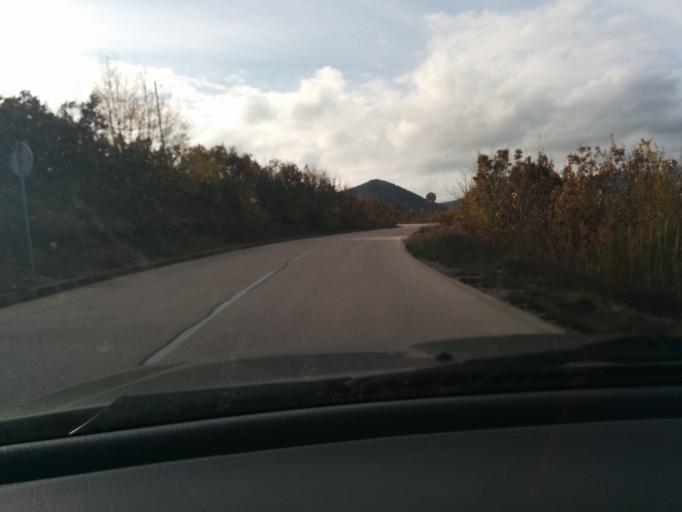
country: HR
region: Splitsko-Dalmatinska
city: Hrvace
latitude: 43.7567
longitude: 16.5779
